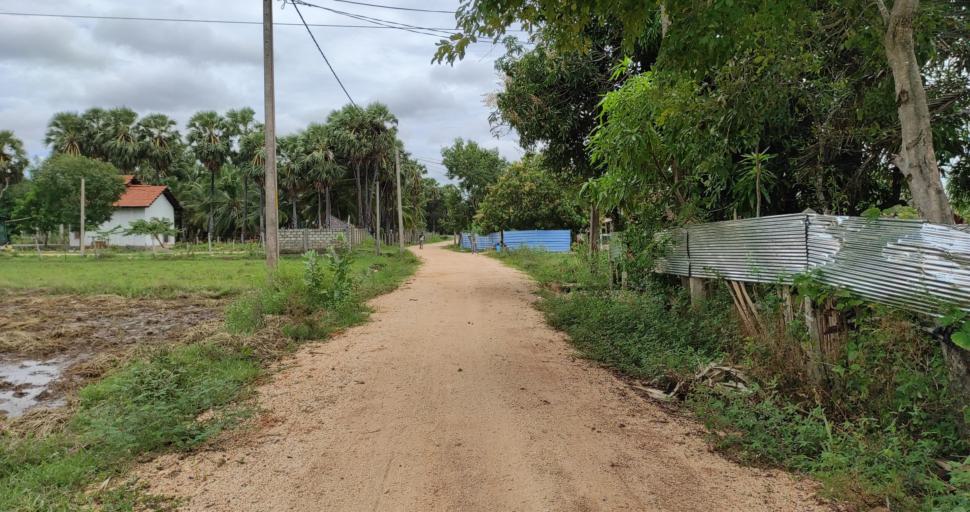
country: LK
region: Eastern Province
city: Trincomalee
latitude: 8.4447
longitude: 81.0532
